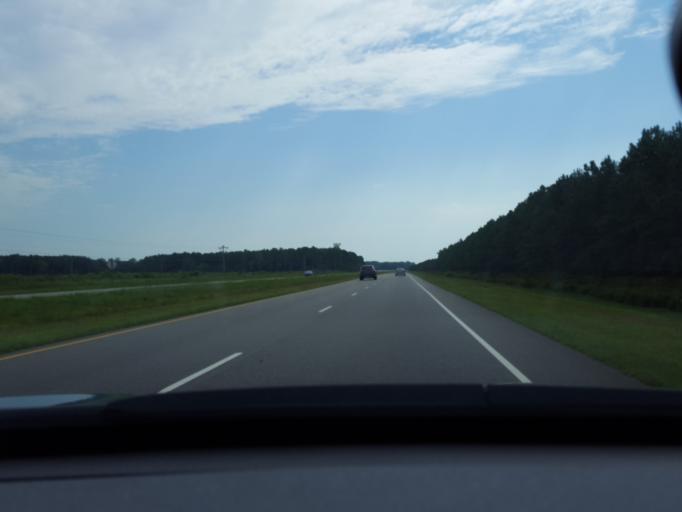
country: US
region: North Carolina
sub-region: Chowan County
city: Edenton
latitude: 36.0377
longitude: -76.7367
